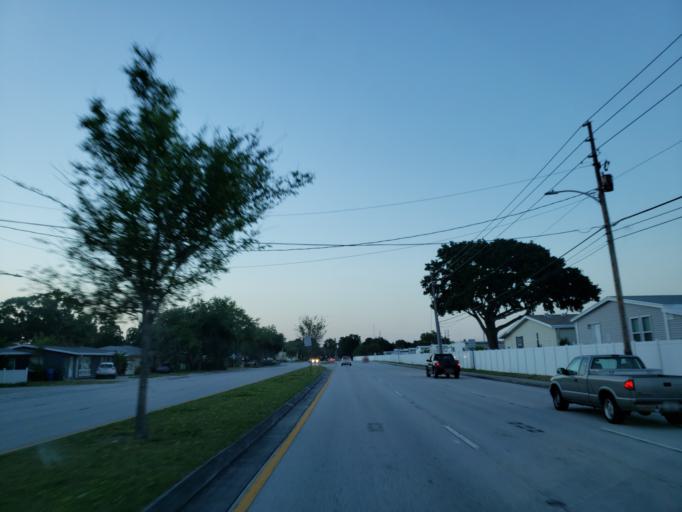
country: US
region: Florida
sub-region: Pinellas County
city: Largo
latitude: 27.9055
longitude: -82.7953
